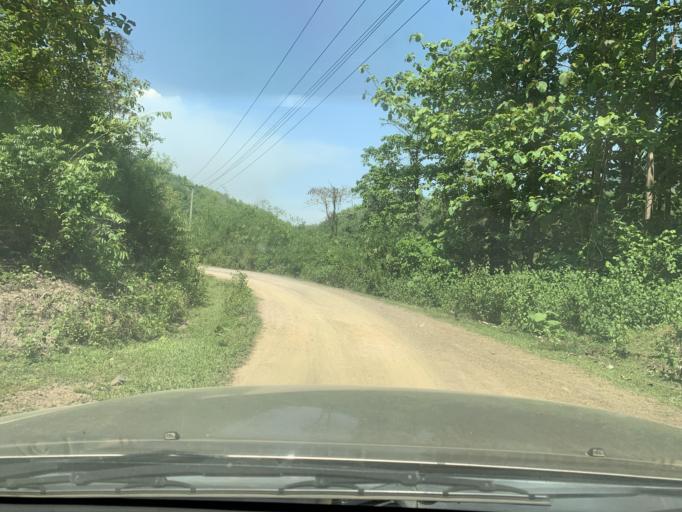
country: LA
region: Louangphabang
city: Louangphabang
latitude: 19.9103
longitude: 102.2595
